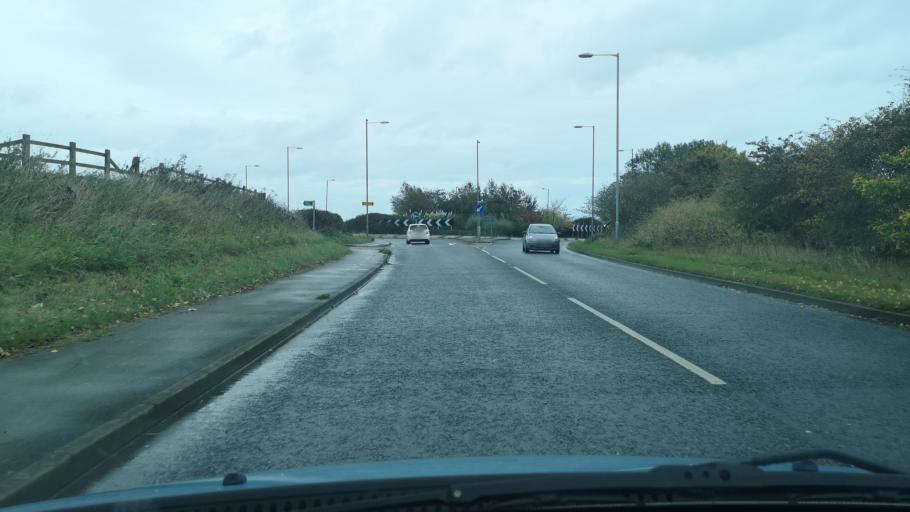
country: GB
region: England
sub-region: City and Borough of Wakefield
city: Hemsworth
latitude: 53.6267
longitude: -1.3394
